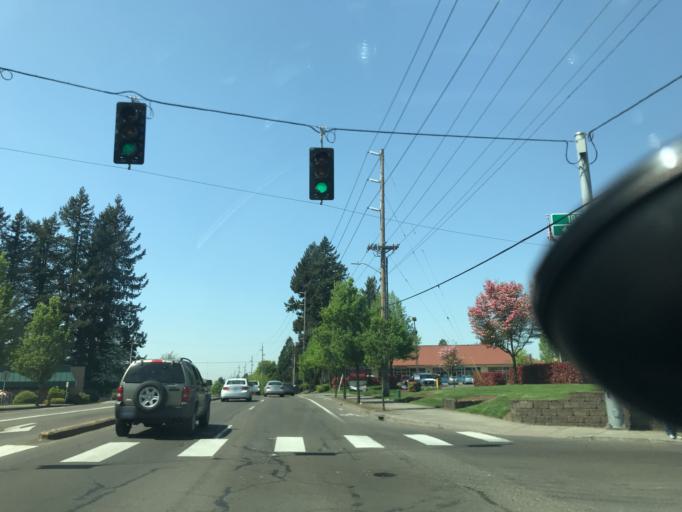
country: US
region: Oregon
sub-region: Multnomah County
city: Gresham
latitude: 45.4904
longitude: -122.4755
